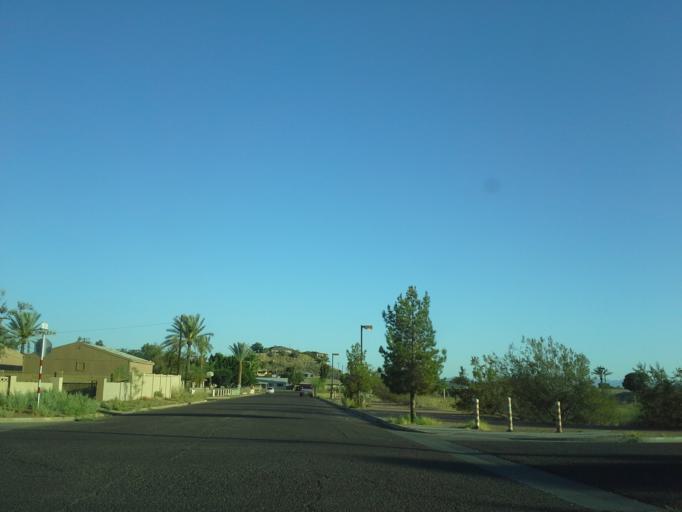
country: US
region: Arizona
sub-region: Maricopa County
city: Phoenix
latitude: 33.5661
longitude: -112.0589
